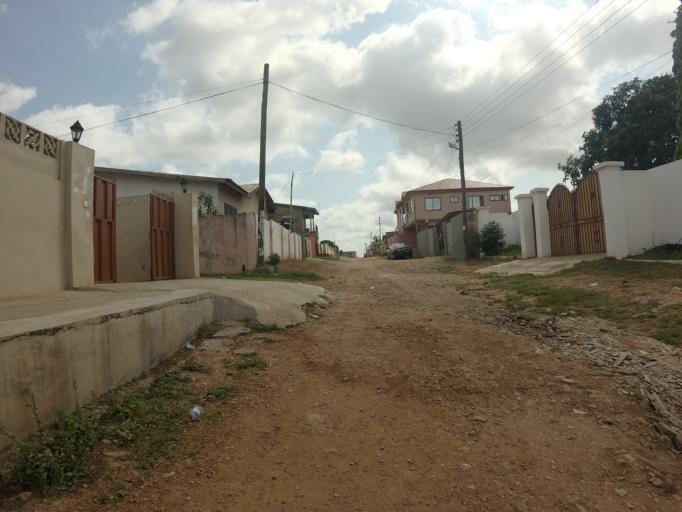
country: GH
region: Greater Accra
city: Dome
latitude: 5.6169
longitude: -0.2441
